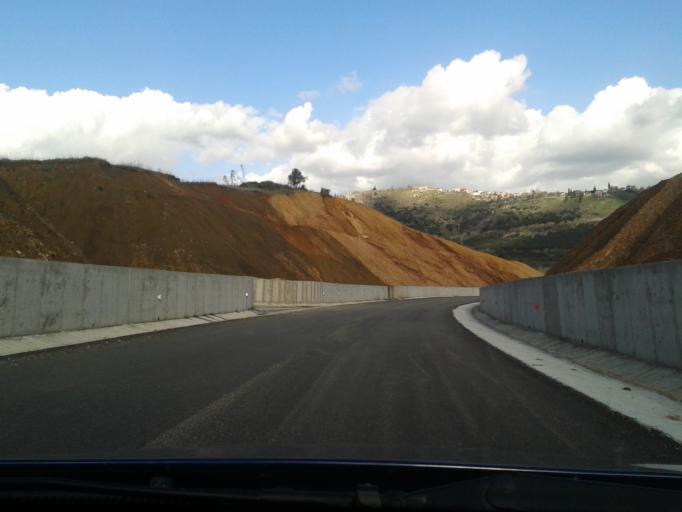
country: GR
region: West Greece
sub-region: Nomos Aitolias kai Akarnanias
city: Fitiai
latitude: 38.6863
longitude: 21.1700
